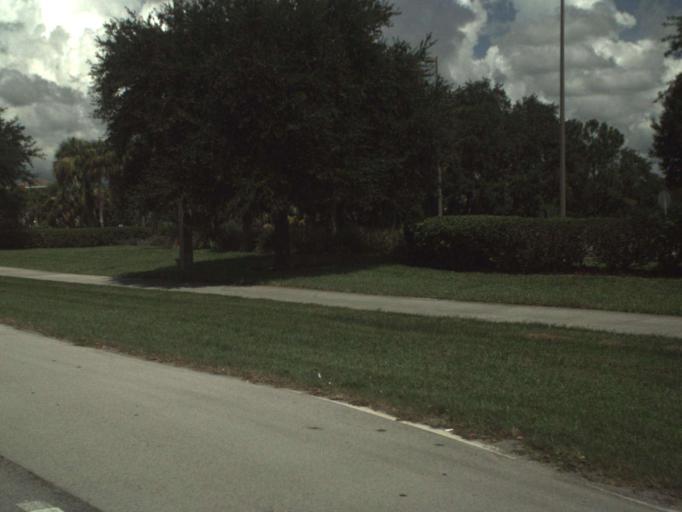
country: US
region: Florida
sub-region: Saint Lucie County
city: River Park
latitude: 27.3135
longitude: -80.3964
